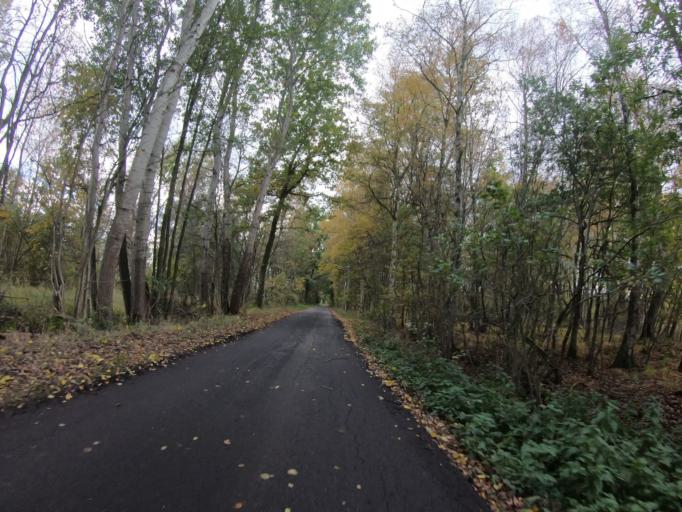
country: DE
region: Lower Saxony
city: Wagenhoff
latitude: 52.5500
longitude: 10.5561
